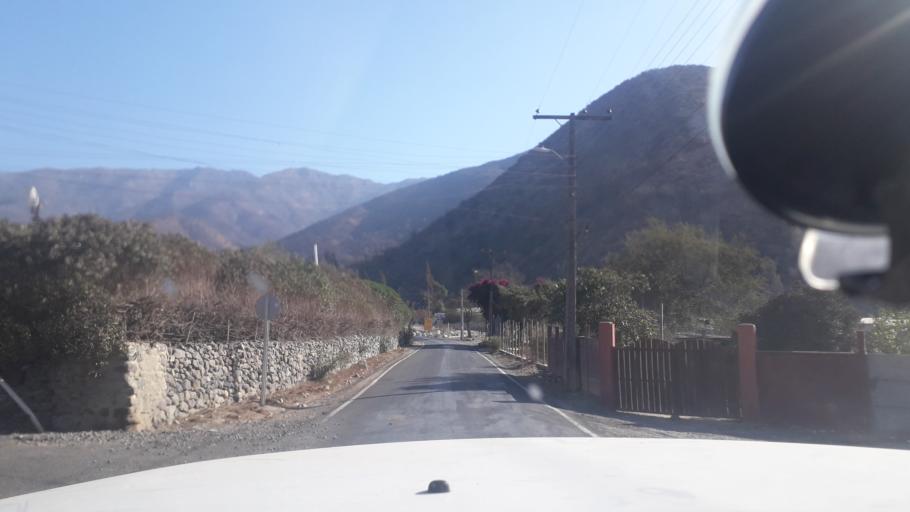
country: CL
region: Valparaiso
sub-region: Provincia de Marga Marga
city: Limache
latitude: -33.0533
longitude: -71.1108
